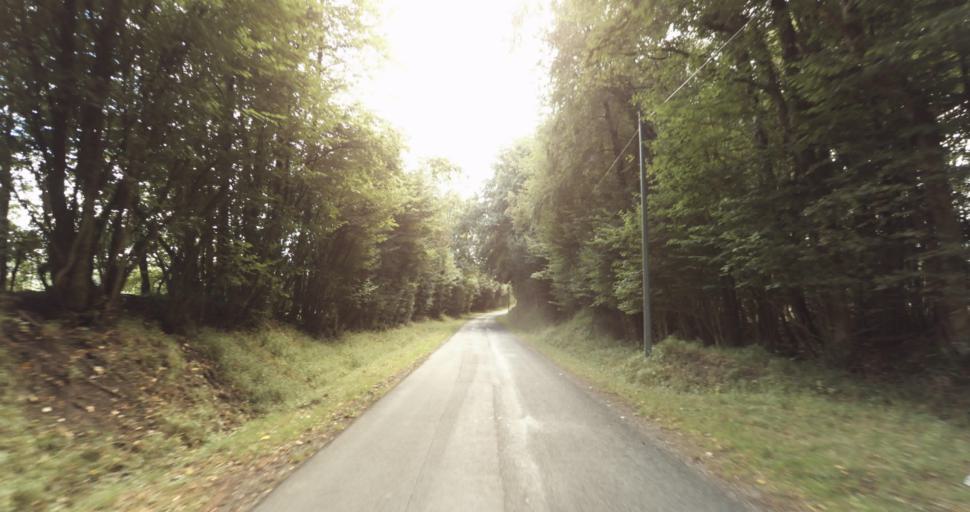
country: FR
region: Lower Normandy
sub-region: Departement de l'Orne
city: Gace
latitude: 48.7809
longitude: 0.3484
